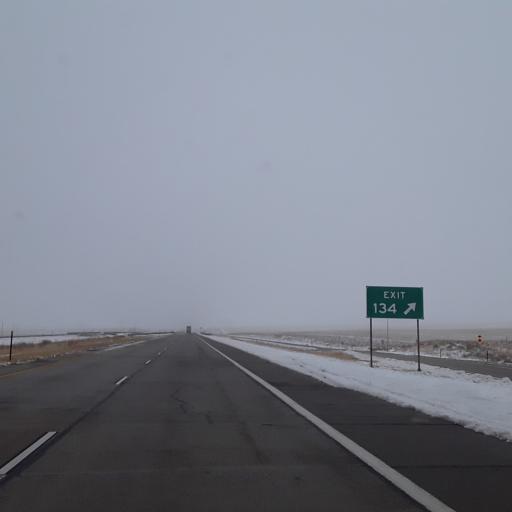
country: US
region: Colorado
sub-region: Logan County
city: Sterling
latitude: 40.7065
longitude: -103.0585
